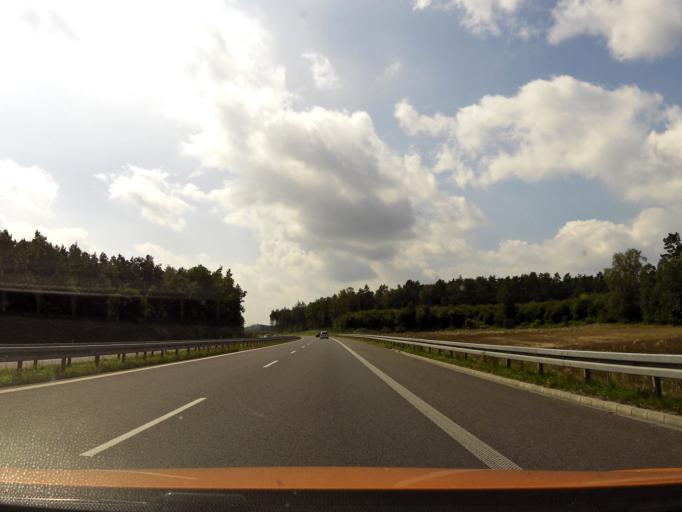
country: PL
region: West Pomeranian Voivodeship
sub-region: Powiat goleniowski
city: Nowogard
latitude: 53.6704
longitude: 15.0780
